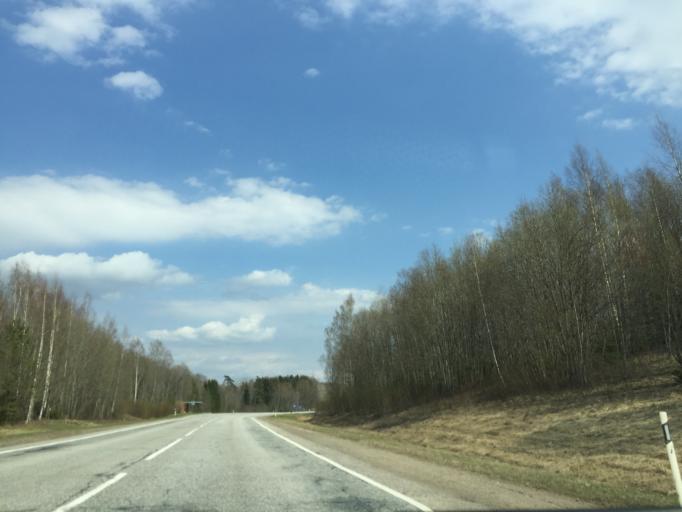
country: LV
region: Apes Novads
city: Ape
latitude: 57.5405
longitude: 26.8307
